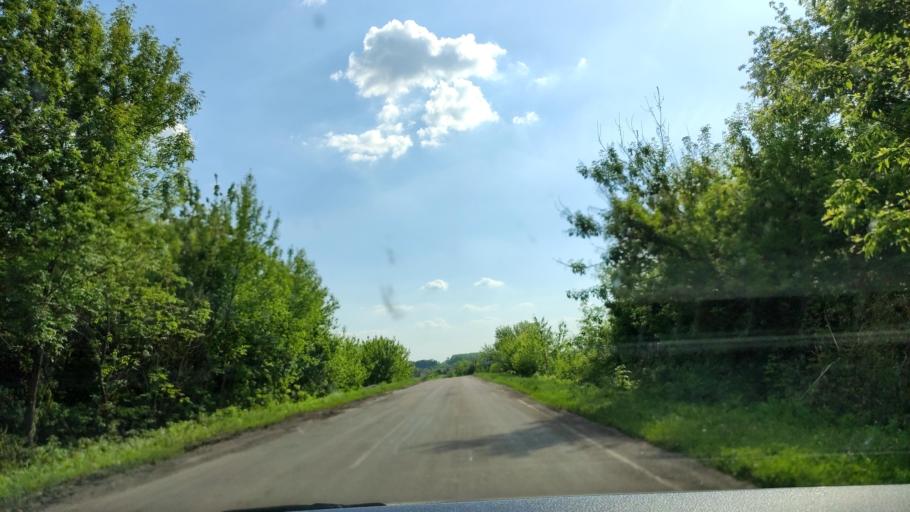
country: RU
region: Voronezj
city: Panino
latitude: 51.6134
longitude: 40.0081
